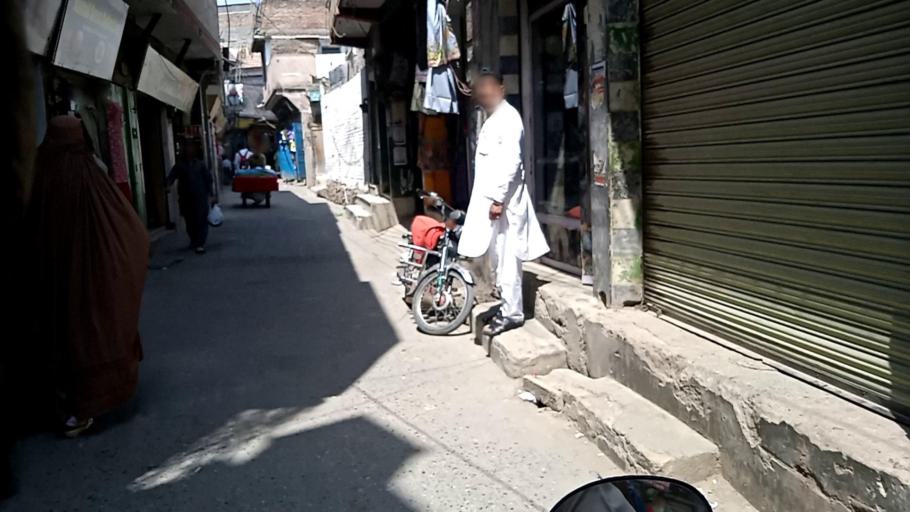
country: PK
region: Khyber Pakhtunkhwa
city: Mingora
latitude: 34.7760
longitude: 72.3535
